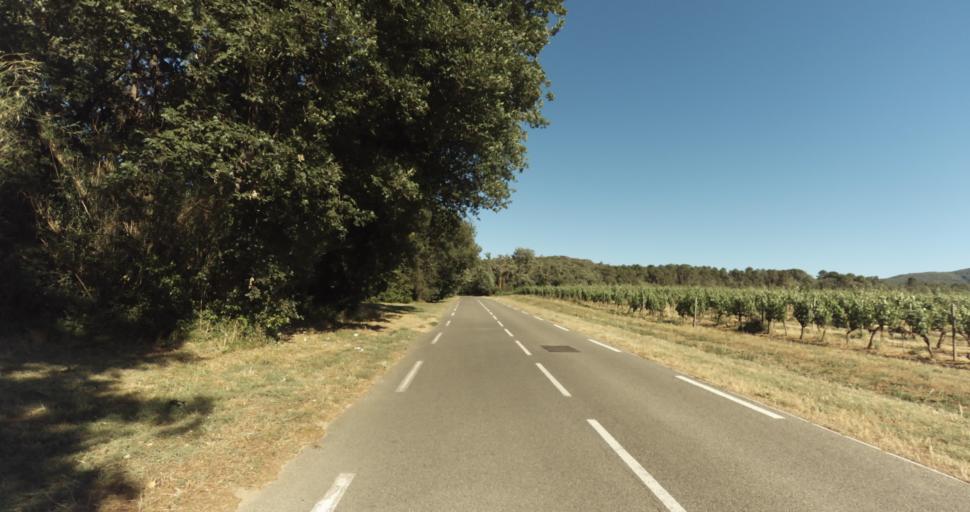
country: FR
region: Provence-Alpes-Cote d'Azur
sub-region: Departement du Var
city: Gassin
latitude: 43.2527
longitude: 6.5961
